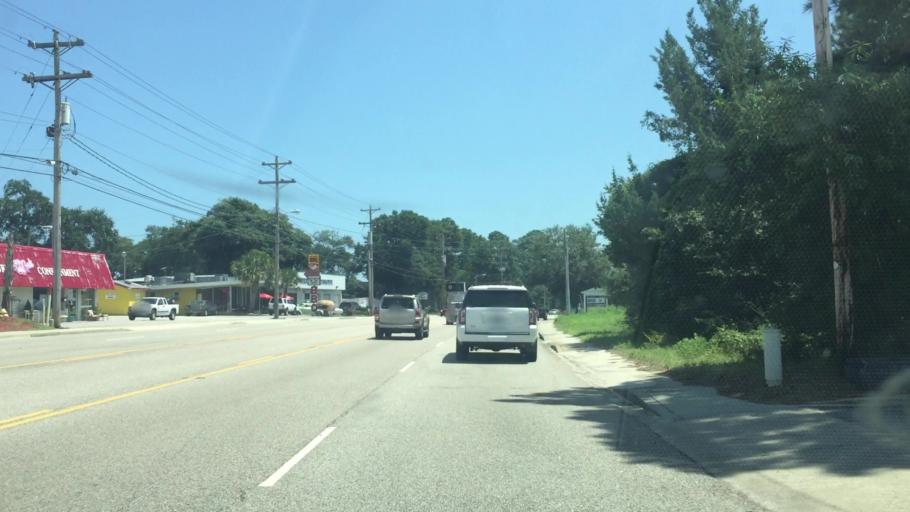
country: US
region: South Carolina
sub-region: Horry County
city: North Myrtle Beach
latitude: 33.8402
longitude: -78.6458
